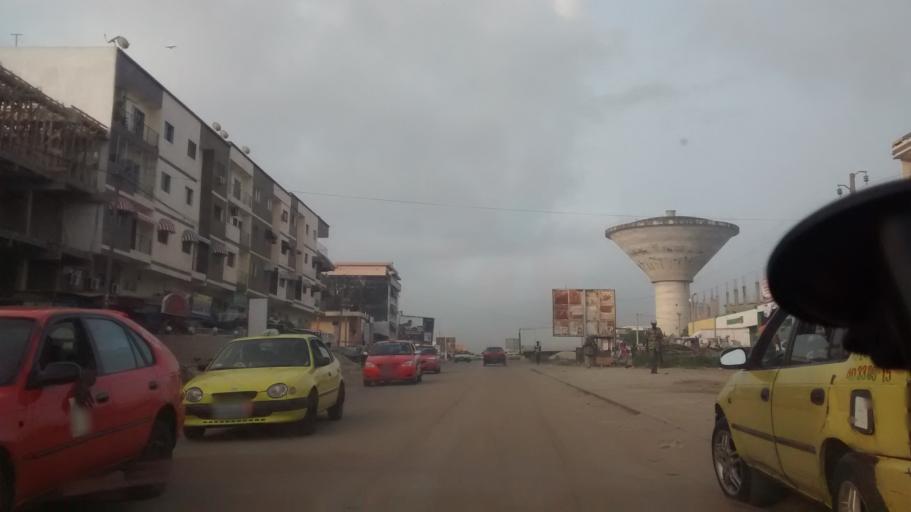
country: CI
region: Lagunes
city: Abobo
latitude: 5.4134
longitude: -3.9800
